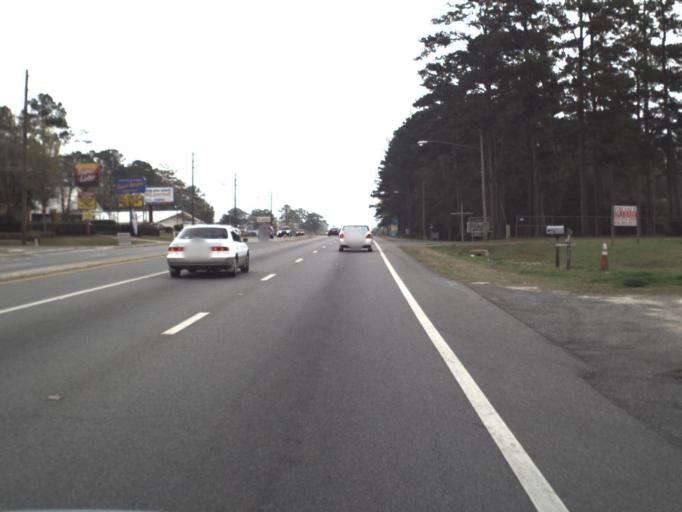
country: US
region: Florida
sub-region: Leon County
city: Tallahassee
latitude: 30.4277
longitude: -84.2212
